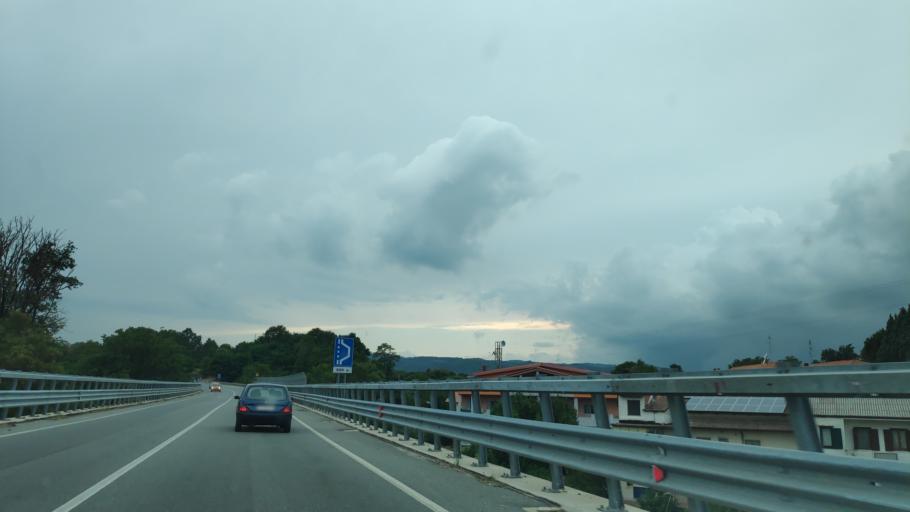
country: IT
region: Calabria
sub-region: Provincia di Catanzaro
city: Chiaravalle Centrale
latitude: 38.6722
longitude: 16.4081
